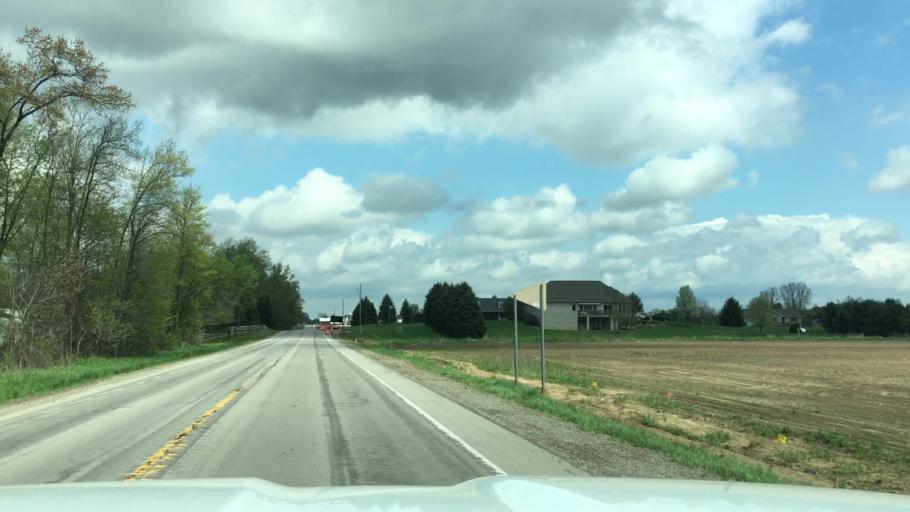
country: US
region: Michigan
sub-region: Ingham County
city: Stockbridge
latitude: 42.4566
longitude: -84.1900
